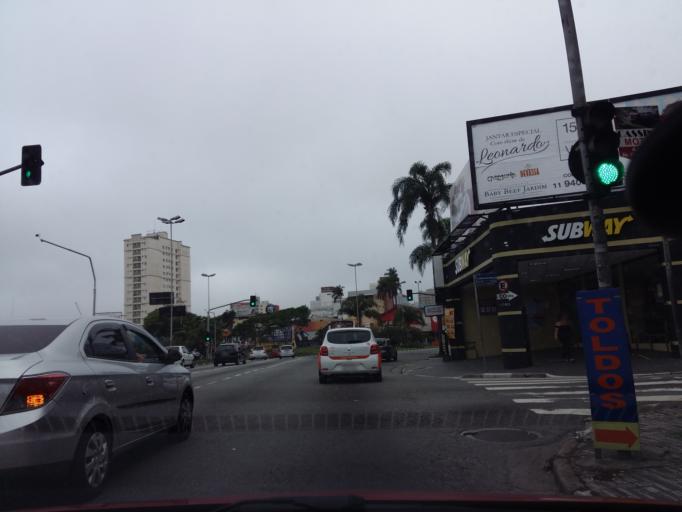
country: BR
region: Sao Paulo
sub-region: Santo Andre
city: Santo Andre
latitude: -23.6659
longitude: -46.5223
